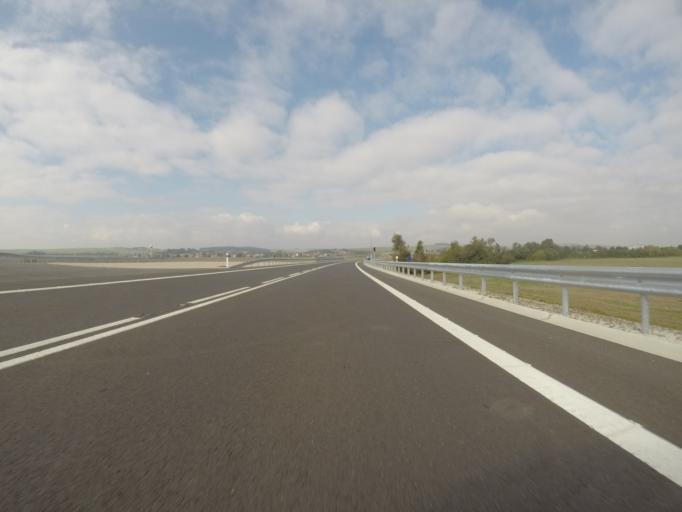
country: SK
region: Nitriansky
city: Banovce nad Bebravou
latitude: 48.7034
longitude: 18.2409
